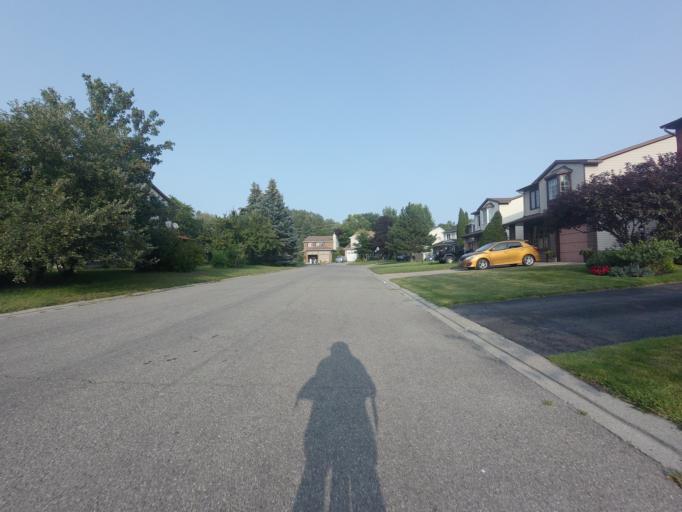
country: CA
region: Ontario
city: Bells Corners
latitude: 45.3371
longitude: -75.7578
